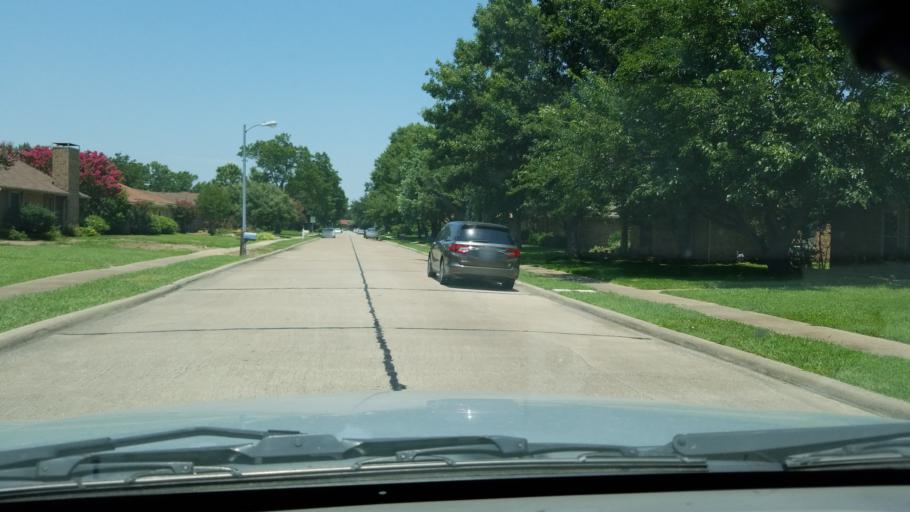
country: US
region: Texas
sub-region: Dallas County
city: Coppell
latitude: 32.9637
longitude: -96.9911
